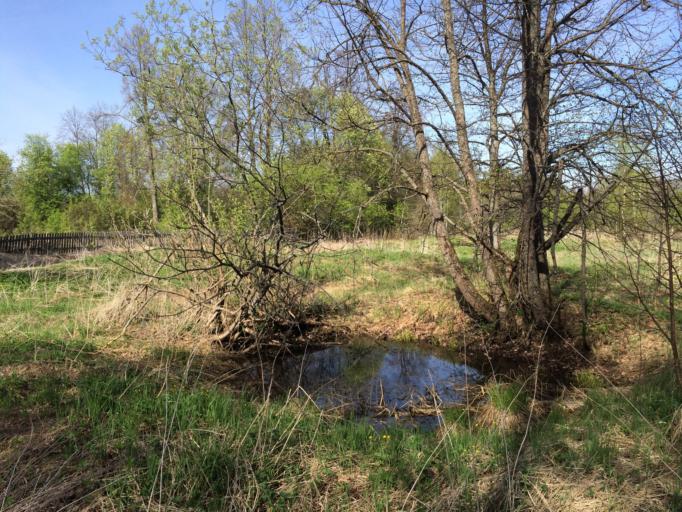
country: RU
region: Jaroslavl
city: Tutayev
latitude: 58.1263
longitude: 39.7967
